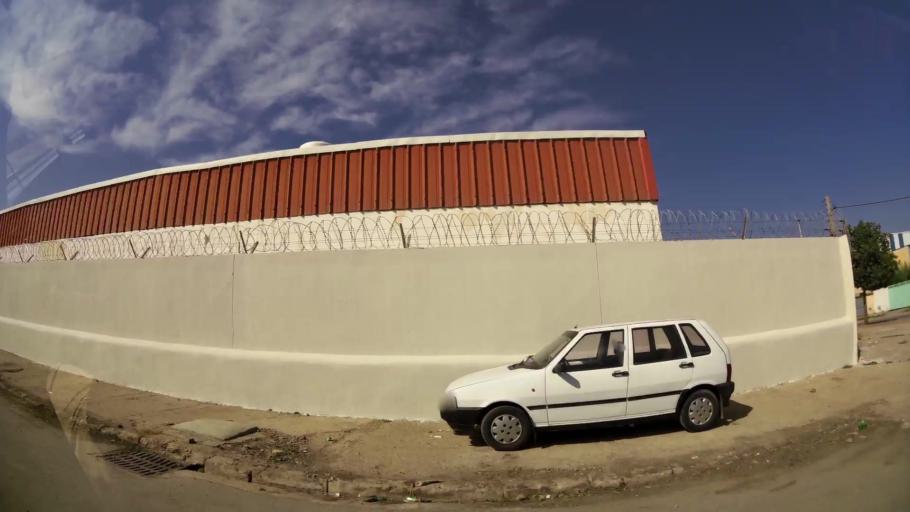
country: MA
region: Oriental
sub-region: Oujda-Angad
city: Oujda
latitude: 34.7046
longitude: -1.8905
